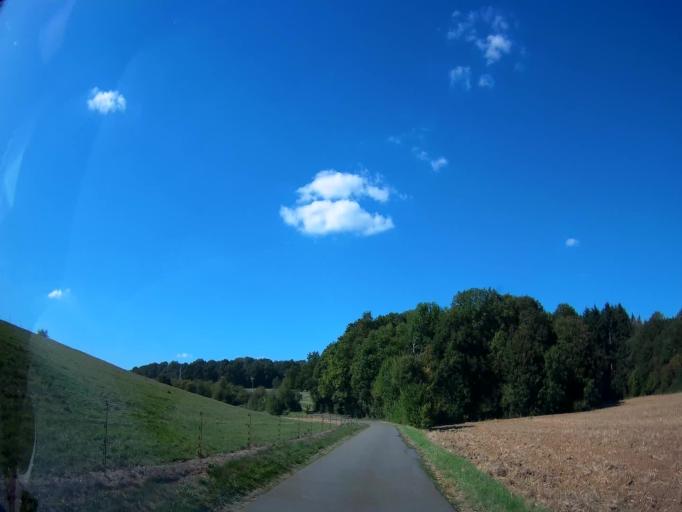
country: BE
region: Wallonia
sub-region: Province de Namur
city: Houyet
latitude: 50.2307
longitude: 4.9821
